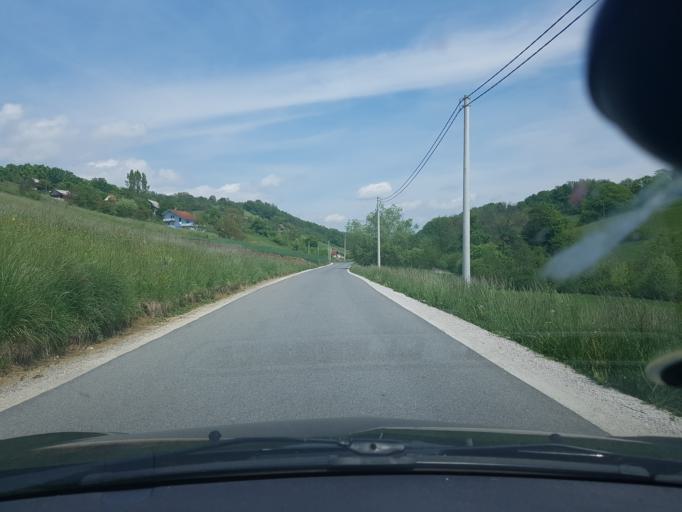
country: HR
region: Krapinsko-Zagorska
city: Pregrada
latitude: 46.1935
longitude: 15.7239
